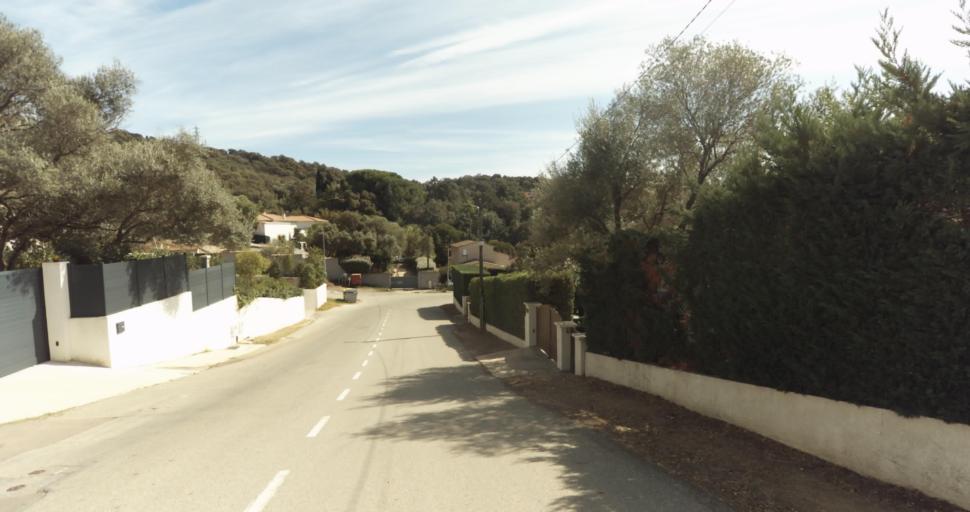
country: FR
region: Corsica
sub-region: Departement de la Corse-du-Sud
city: Ajaccio
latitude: 41.9410
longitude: 8.7645
